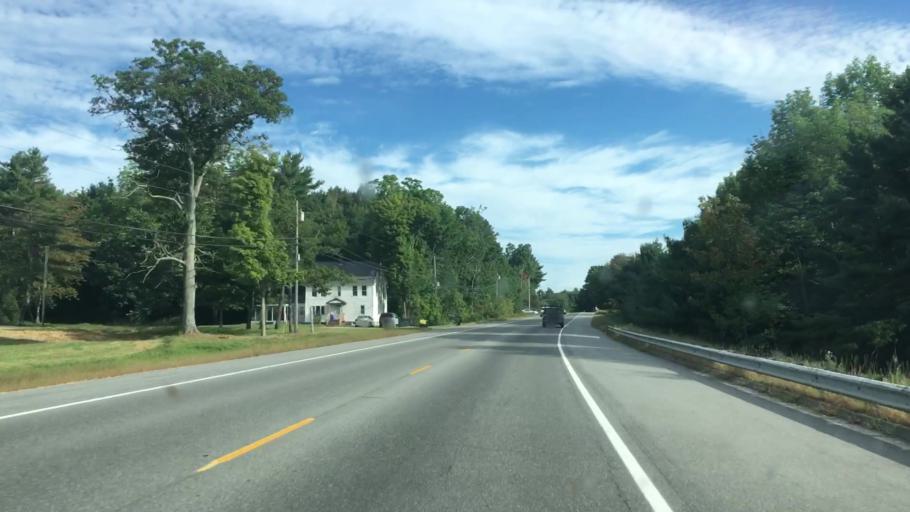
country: US
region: Maine
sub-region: Cumberland County
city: Cumberland Center
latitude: 43.7613
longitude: -70.3015
